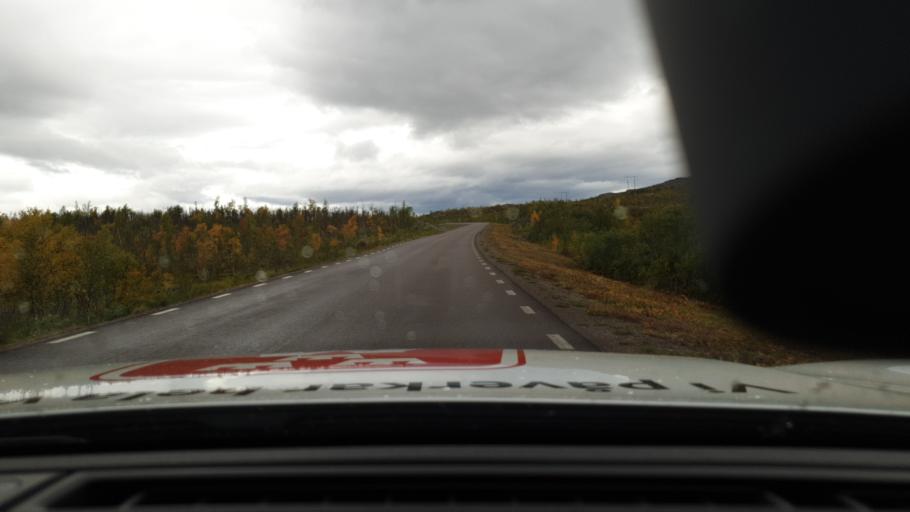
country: NO
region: Troms
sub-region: Bardu
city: Setermoen
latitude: 68.4266
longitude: 18.3408
